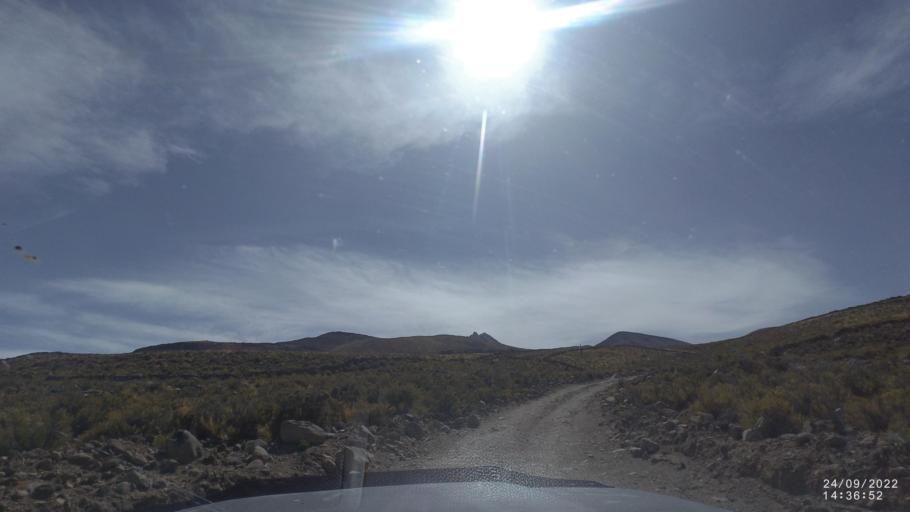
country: BO
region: Potosi
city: Colchani
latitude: -19.8541
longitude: -67.5809
